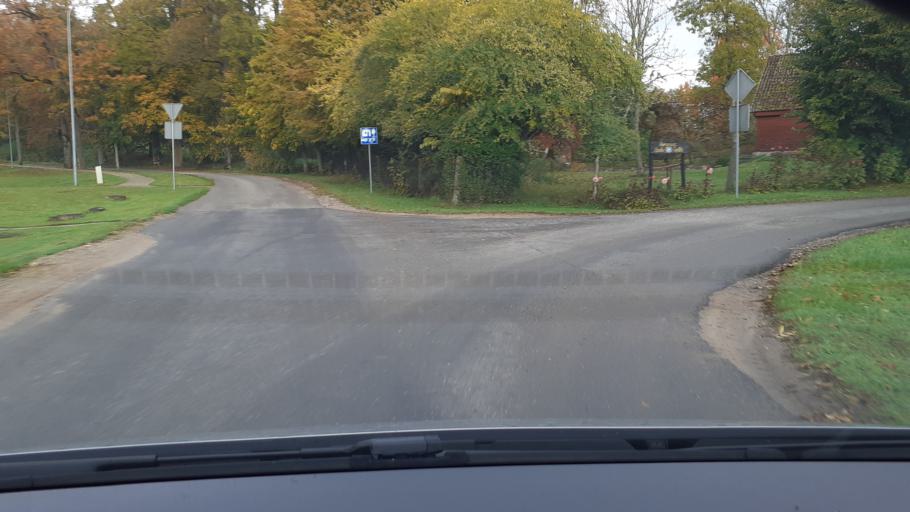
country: LV
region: Kuldigas Rajons
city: Kuldiga
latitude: 57.0181
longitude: 21.9119
